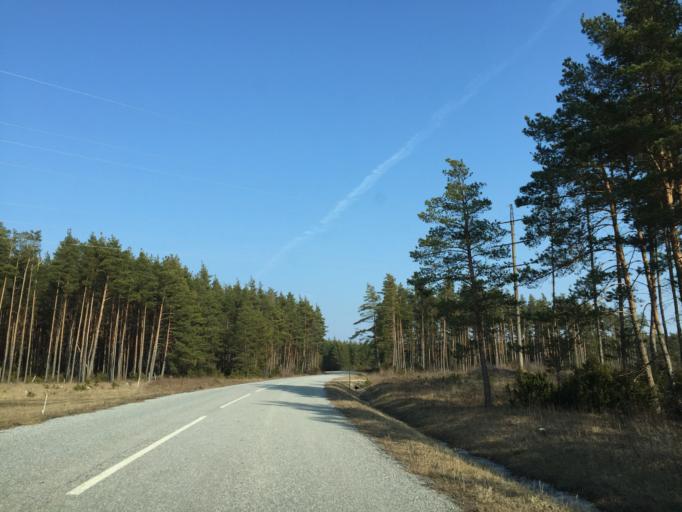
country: EE
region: Saare
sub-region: Orissaare vald
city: Orissaare
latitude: 58.5670
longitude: 23.3494
